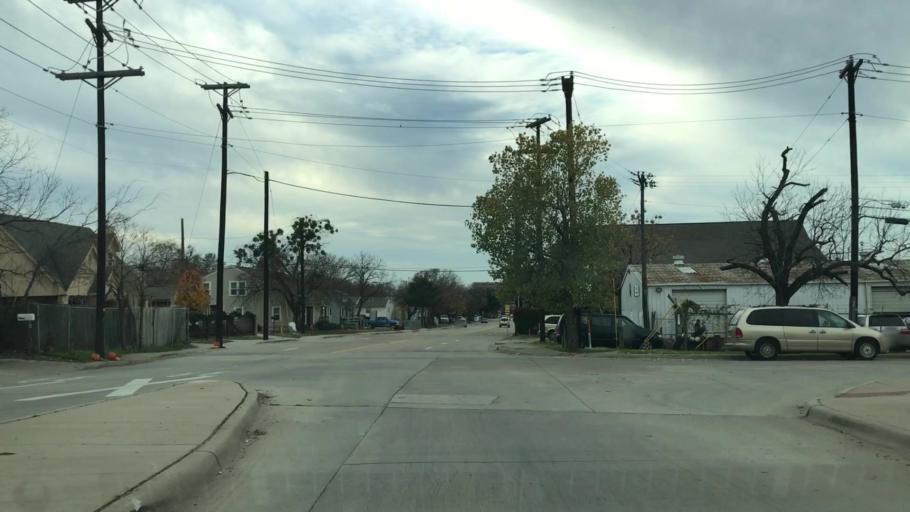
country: US
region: Texas
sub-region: Dallas County
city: University Park
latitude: 32.8418
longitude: -96.8601
